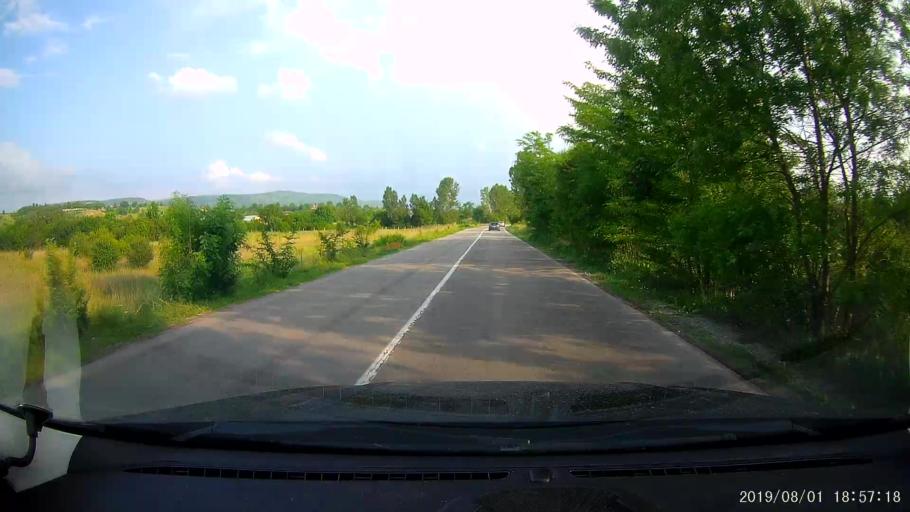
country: BG
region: Shumen
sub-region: Obshtina Smyadovo
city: Smyadovo
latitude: 43.1494
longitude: 27.0223
